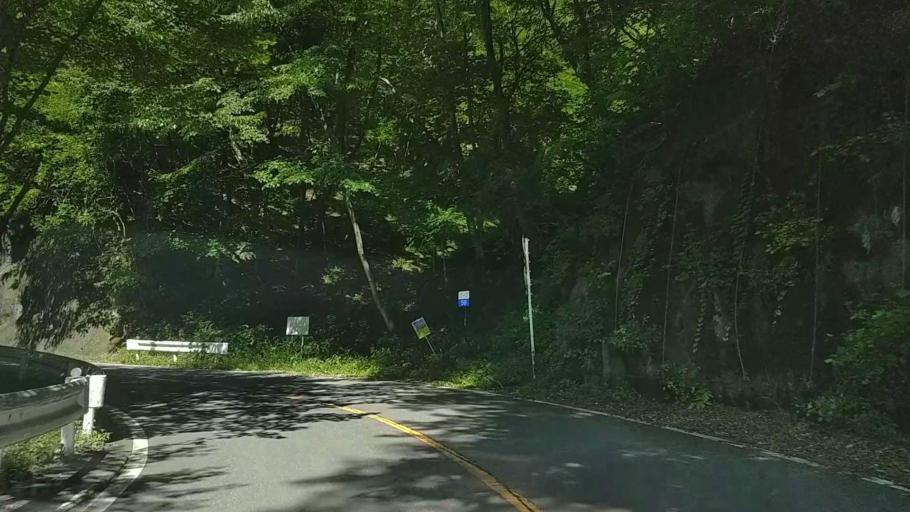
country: JP
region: Gunma
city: Annaka
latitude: 36.3542
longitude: 138.6932
